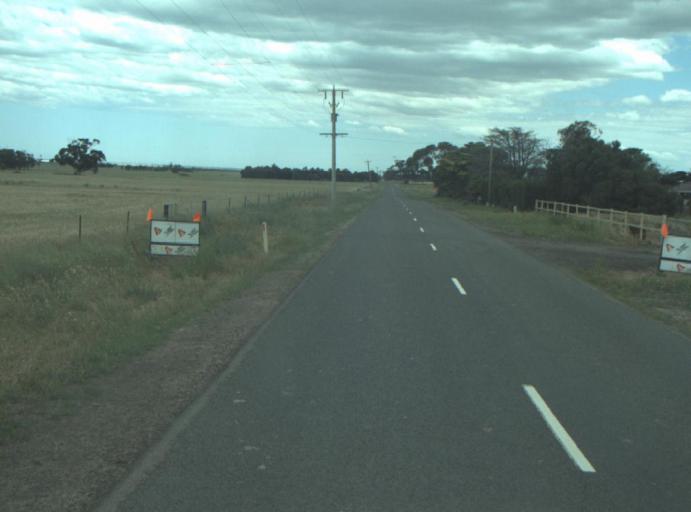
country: AU
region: Victoria
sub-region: Wyndham
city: Little River
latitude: -37.9496
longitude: 144.4654
